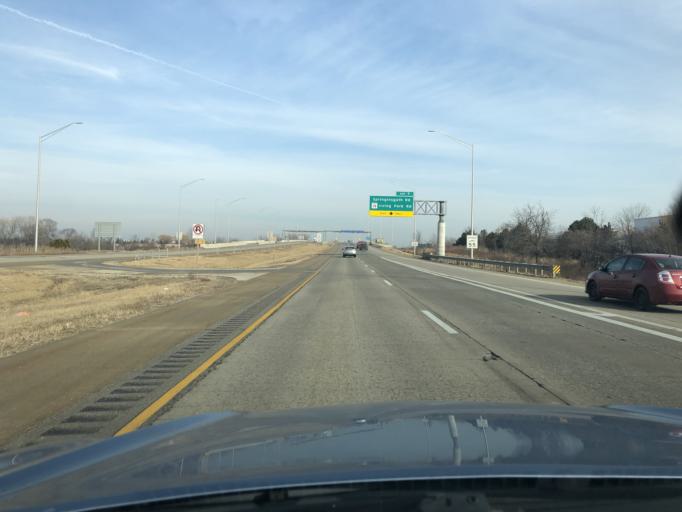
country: US
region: Illinois
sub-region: DuPage County
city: Hanover Park
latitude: 41.9849
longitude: -88.1327
